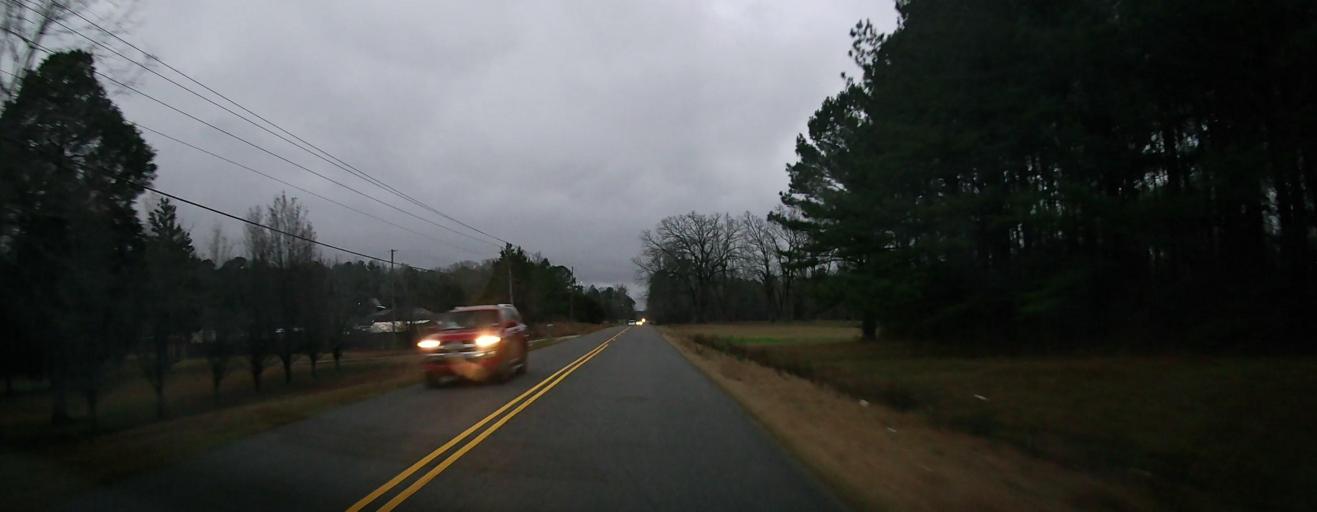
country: US
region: Alabama
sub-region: Tuscaloosa County
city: Vance
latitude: 33.1432
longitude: -87.2298
